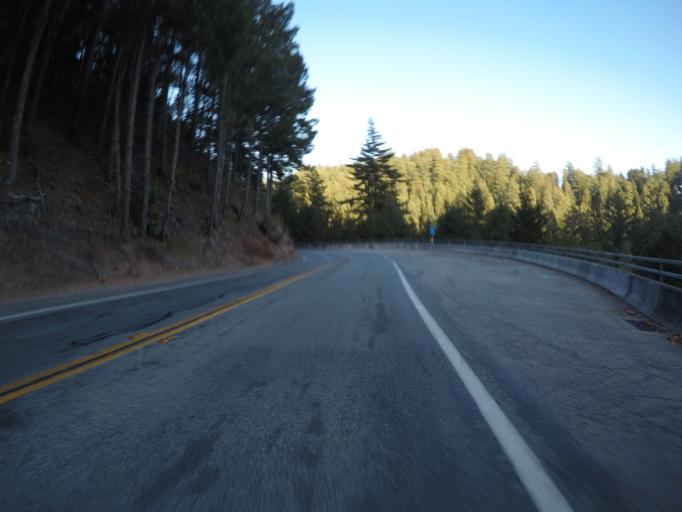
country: US
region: California
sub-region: Santa Cruz County
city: Mount Hermon
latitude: 37.0242
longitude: -122.0599
